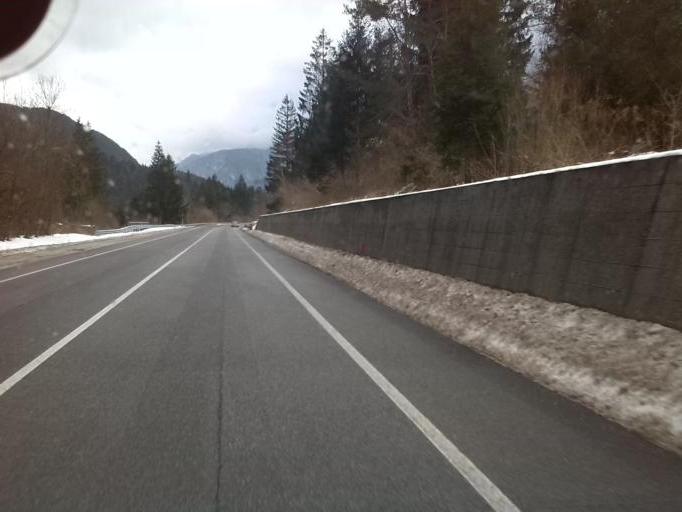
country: IT
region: Friuli Venezia Giulia
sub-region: Provincia di Udine
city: Pontebba
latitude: 46.5083
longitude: 13.3564
